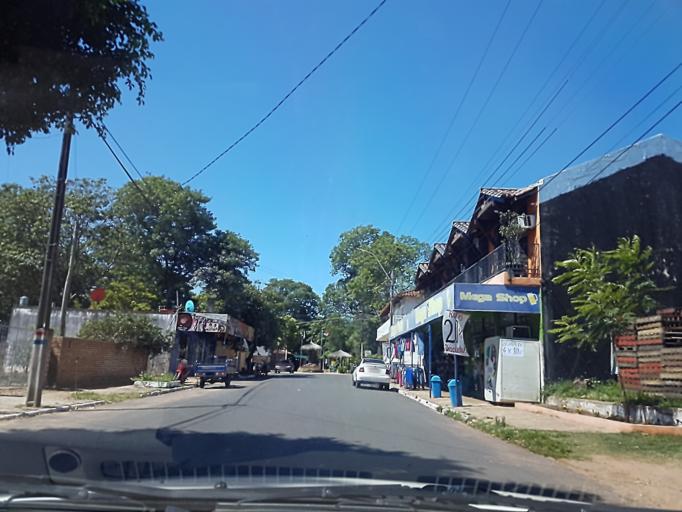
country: PY
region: Cordillera
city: Atyra
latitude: -25.2795
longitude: -57.1740
